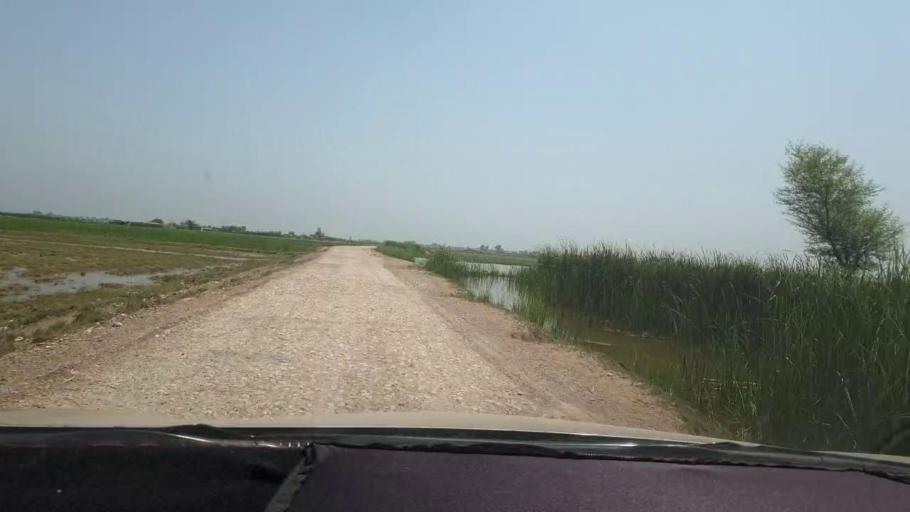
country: PK
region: Sindh
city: Shahdadkot
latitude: 27.8266
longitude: 67.9894
